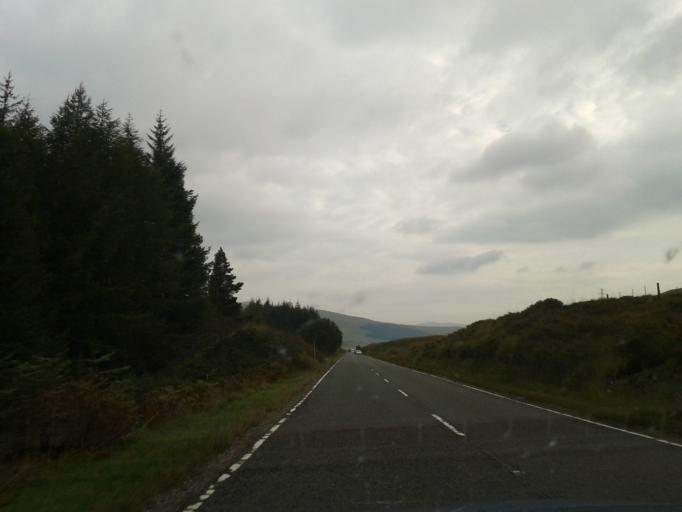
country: GB
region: Scotland
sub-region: Highland
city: Spean Bridge
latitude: 56.5446
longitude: -4.7608
